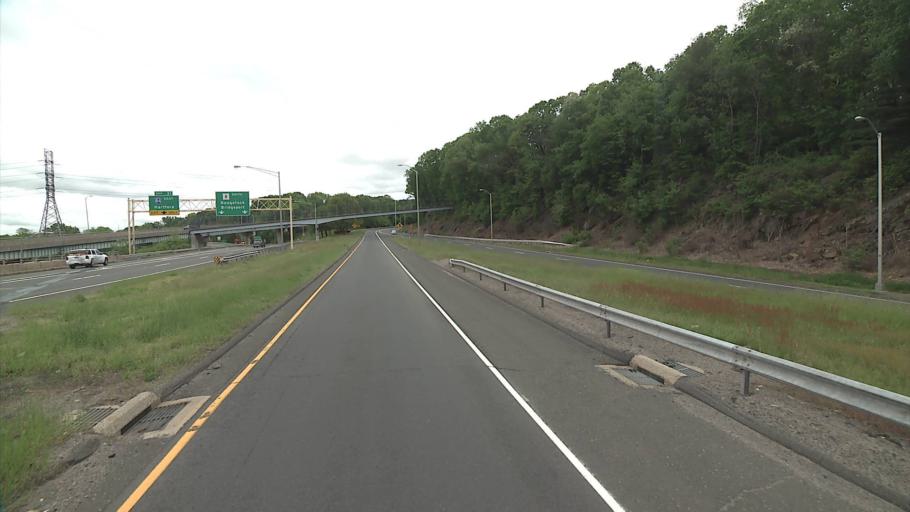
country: US
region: Connecticut
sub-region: New Haven County
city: Waterbury
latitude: 41.5548
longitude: -73.0555
